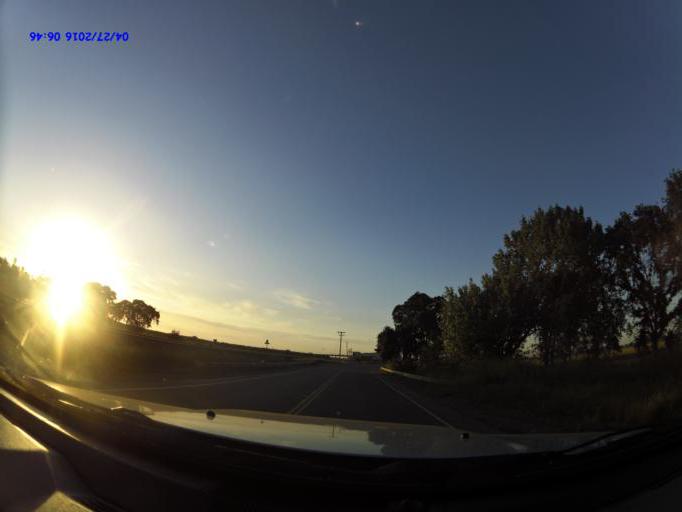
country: US
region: California
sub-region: San Joaquin County
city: Garden Acres
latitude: 37.9162
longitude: -121.1897
